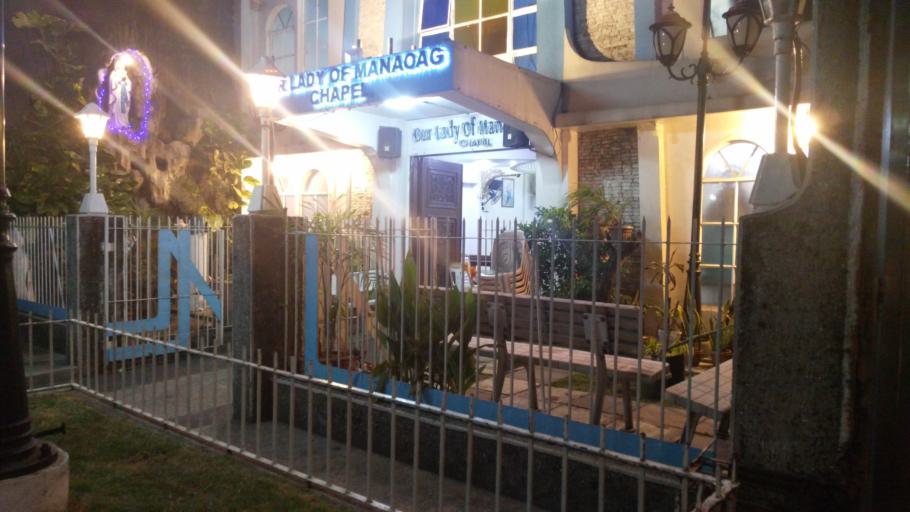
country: PH
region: Metro Manila
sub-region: City of Manila
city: Quiapo
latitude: 14.6023
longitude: 120.9977
